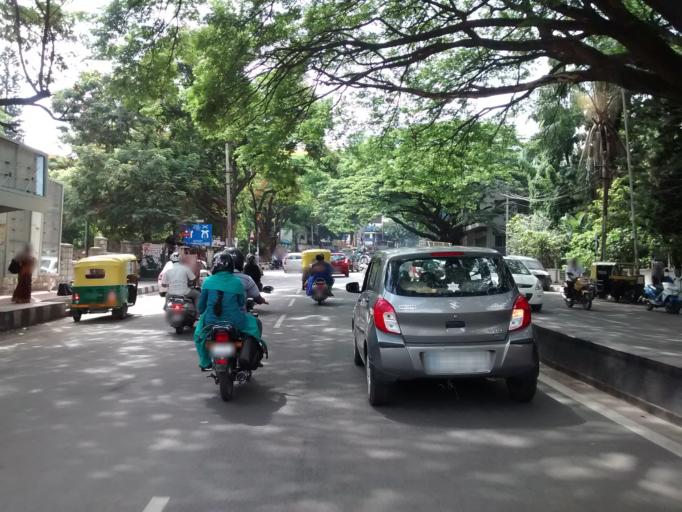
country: IN
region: Karnataka
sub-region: Bangalore Urban
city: Bangalore
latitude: 12.9968
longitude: 77.5538
